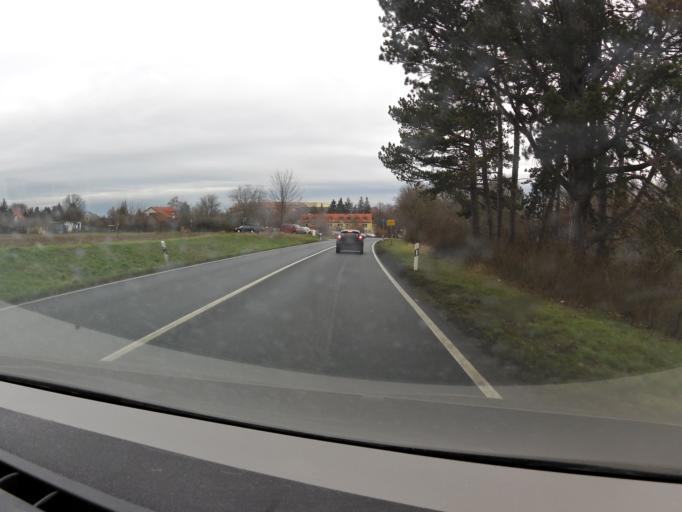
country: DE
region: Saxony-Anhalt
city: Aschersleben
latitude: 51.7432
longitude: 11.4563
